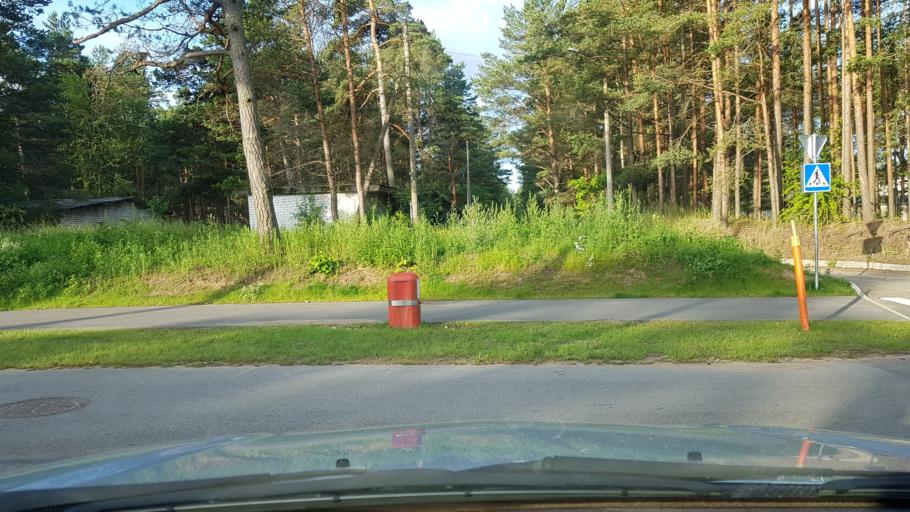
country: EE
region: Ida-Virumaa
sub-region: Narva-Joesuu linn
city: Narva-Joesuu
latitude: 59.4553
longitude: 28.0470
